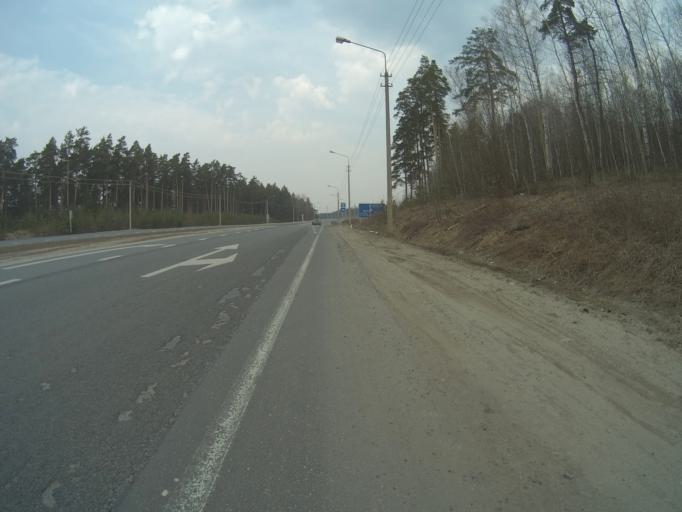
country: RU
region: Vladimir
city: Kommunar
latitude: 56.0512
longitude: 40.4385
